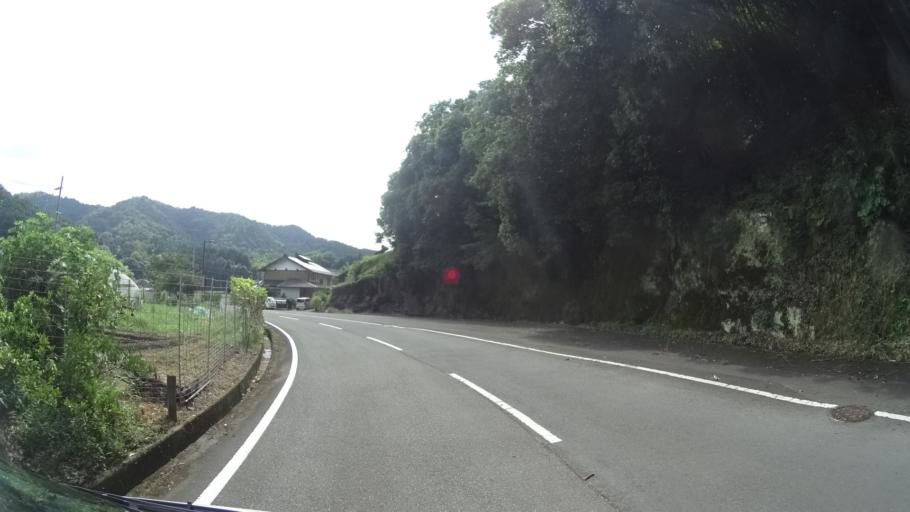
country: JP
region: Kyoto
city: Fukuchiyama
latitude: 35.3753
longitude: 135.1516
